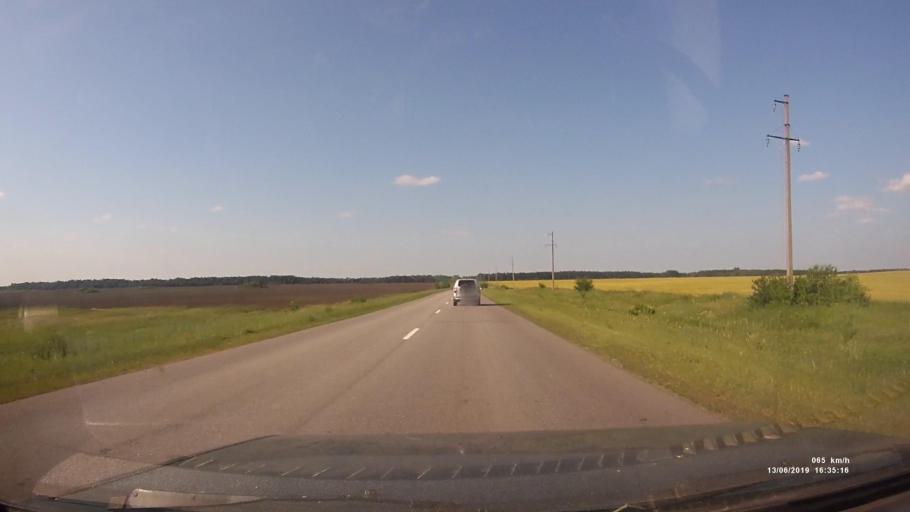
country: RU
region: Rostov
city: Kazanskaya
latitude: 49.8808
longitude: 41.2974
